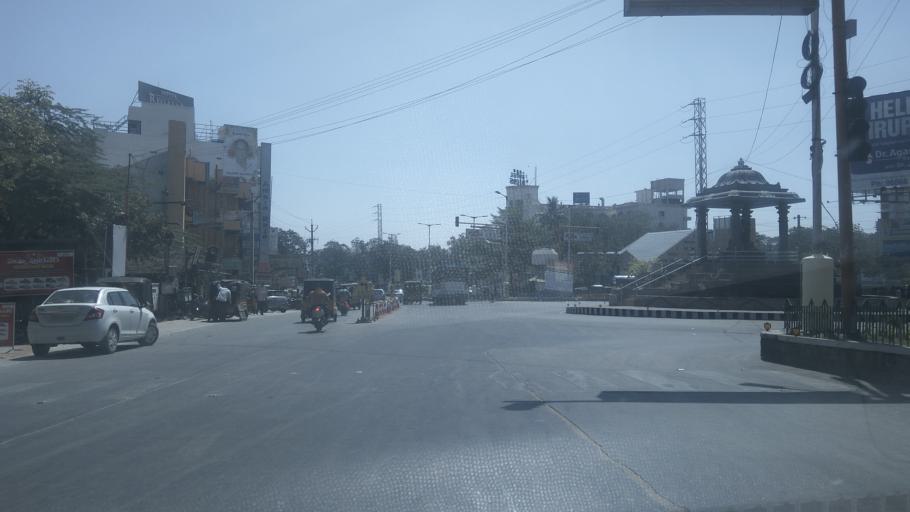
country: IN
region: Andhra Pradesh
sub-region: Chittoor
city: Tirupati
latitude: 13.6265
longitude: 79.4308
